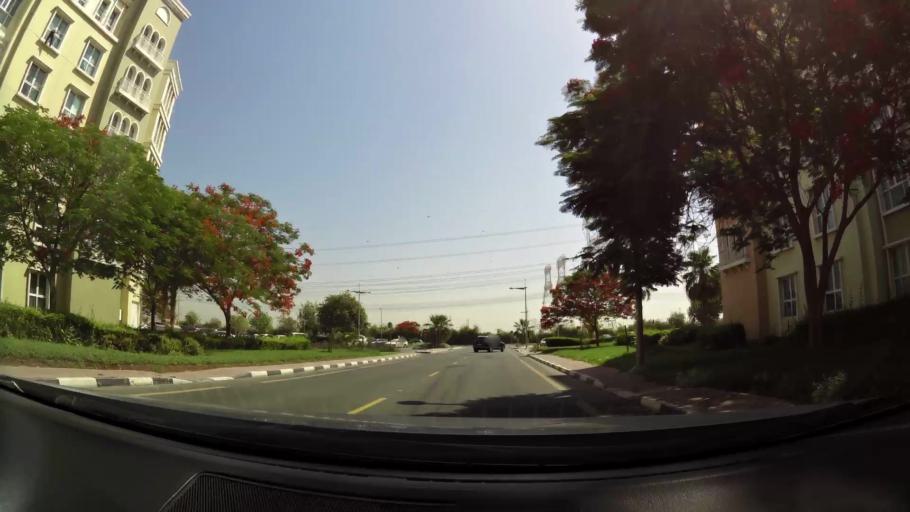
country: AE
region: Dubai
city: Dubai
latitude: 25.0315
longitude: 55.1555
